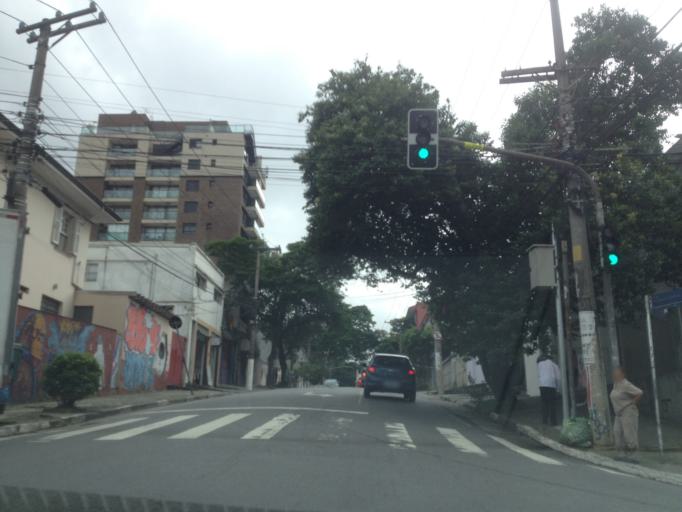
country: BR
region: Sao Paulo
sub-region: Sao Paulo
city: Sao Paulo
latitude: -23.5547
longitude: -46.6925
